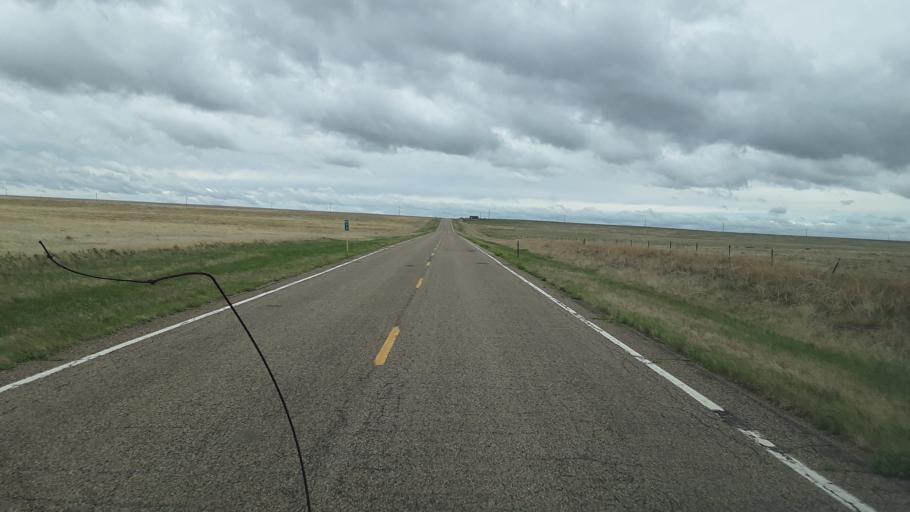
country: US
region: Colorado
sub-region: Lincoln County
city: Hugo
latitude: 38.8511
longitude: -103.6176
